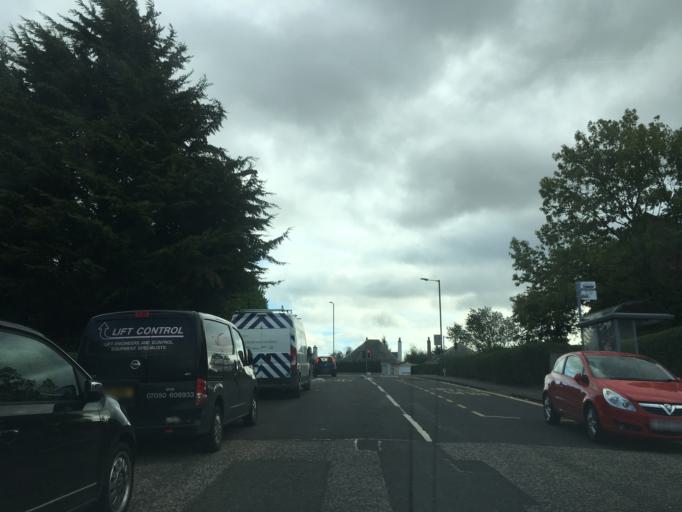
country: GB
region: Scotland
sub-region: Edinburgh
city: Edinburgh
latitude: 55.9615
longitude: -3.2475
